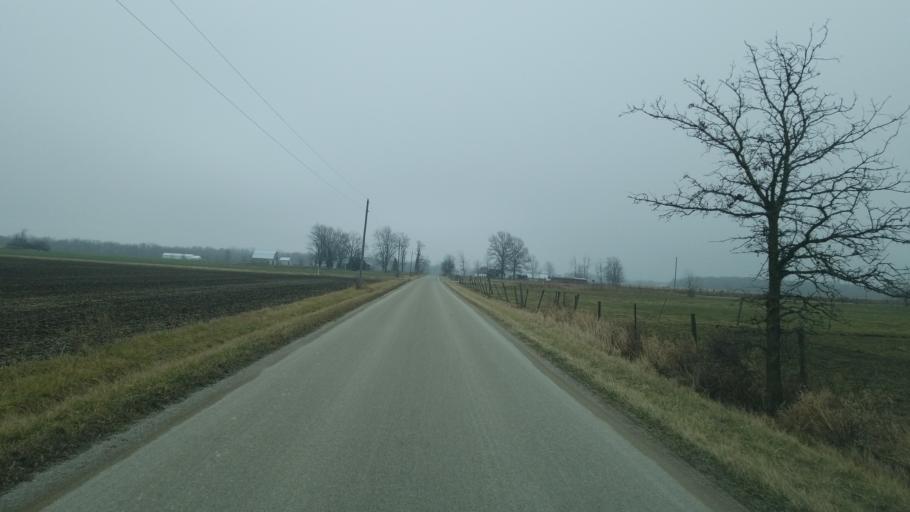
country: US
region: Indiana
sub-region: Adams County
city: Geneva
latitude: 40.5707
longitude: -84.9379
